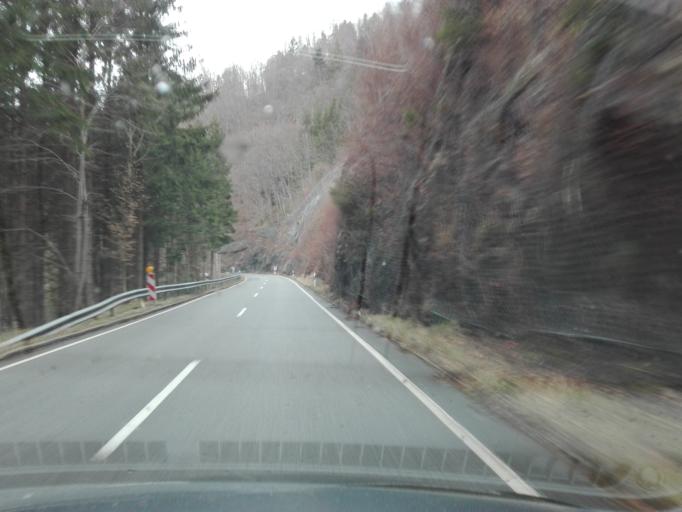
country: DE
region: Bavaria
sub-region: Lower Bavaria
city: Thyrnau
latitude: 48.5919
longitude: 13.5838
